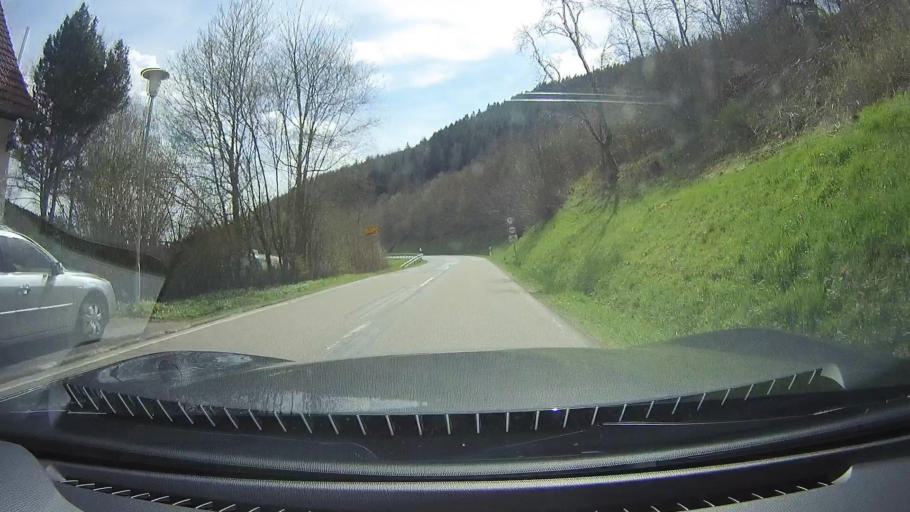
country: DE
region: Hesse
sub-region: Regierungsbezirk Darmstadt
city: Hesseneck
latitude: 49.5656
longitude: 9.0706
